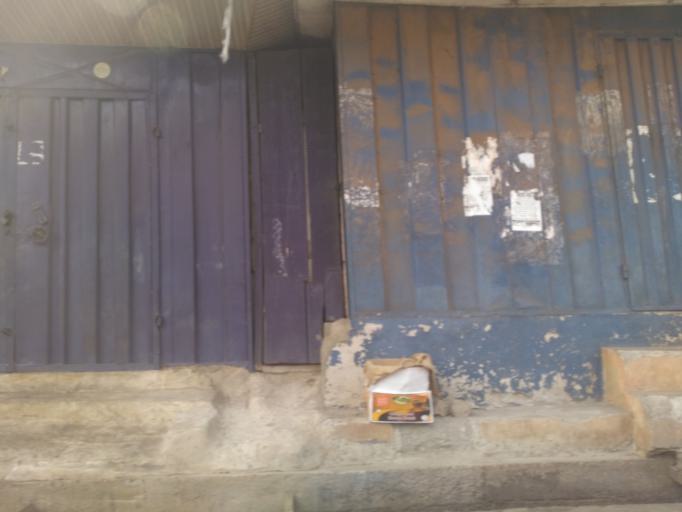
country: GH
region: Ashanti
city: Kumasi
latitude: 6.6959
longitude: -1.6123
